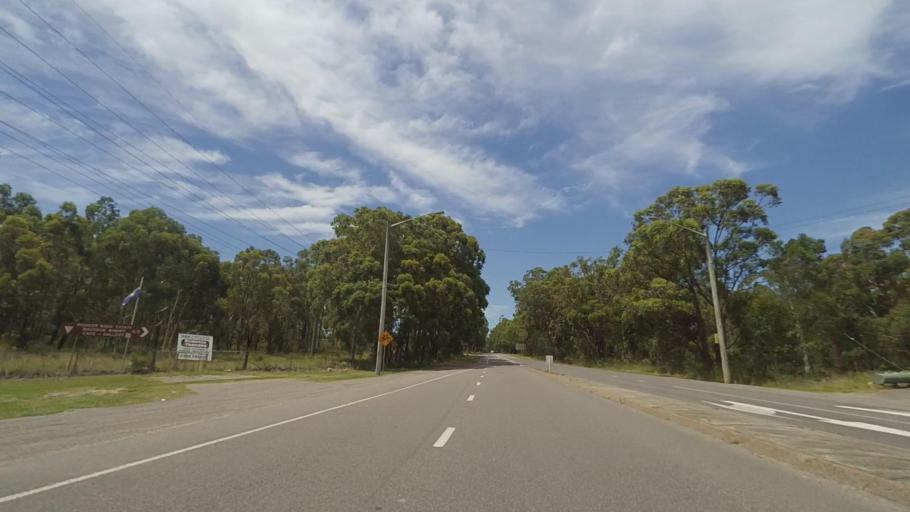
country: AU
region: New South Wales
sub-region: Port Stephens Shire
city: Medowie
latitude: -32.7717
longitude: 151.8603
